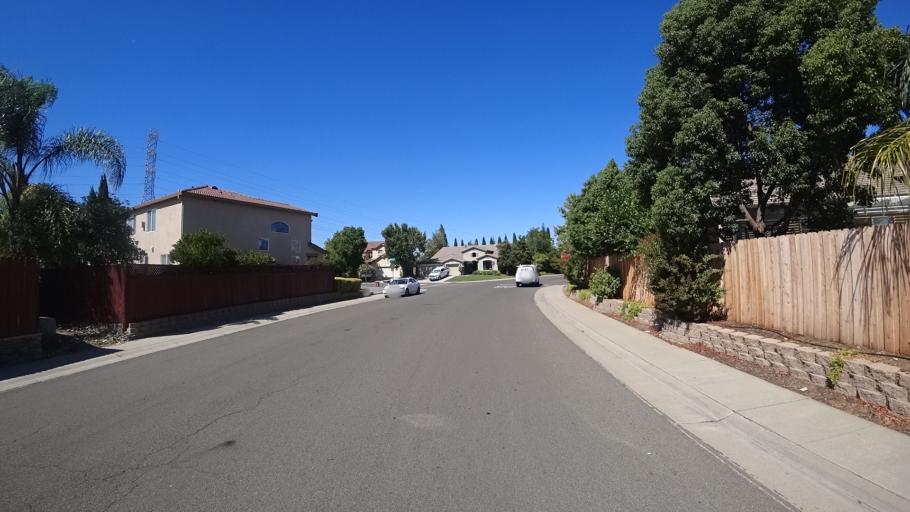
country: US
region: California
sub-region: Sacramento County
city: Elk Grove
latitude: 38.4155
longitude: -121.3490
